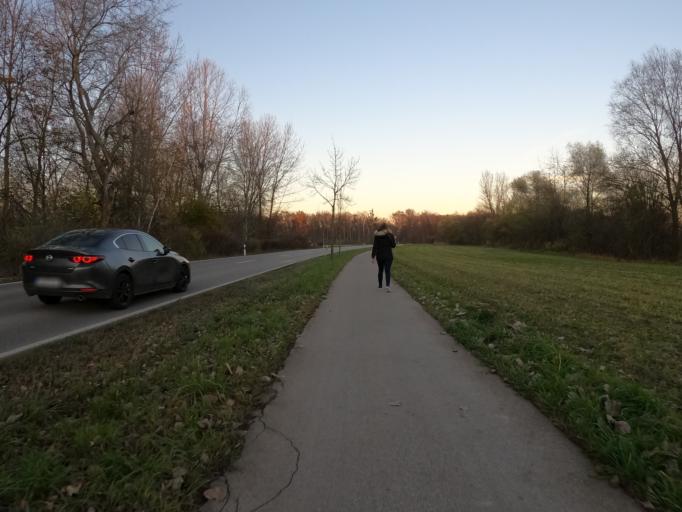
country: DE
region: Bavaria
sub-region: Swabia
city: Nersingen
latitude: 48.4285
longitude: 10.0839
